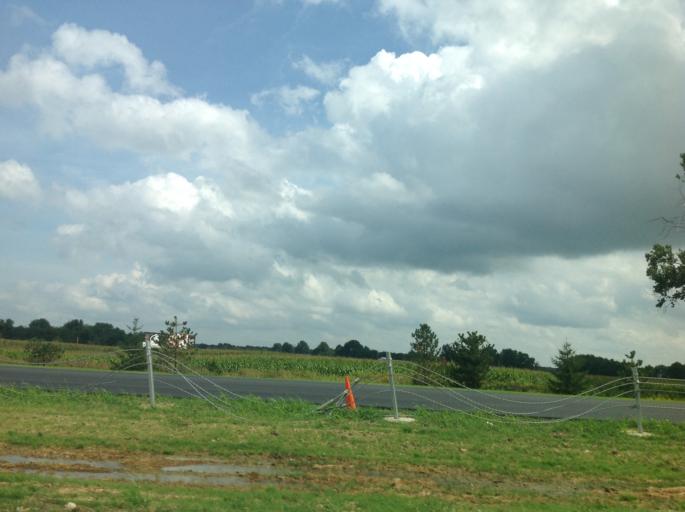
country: US
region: Ohio
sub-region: Delaware County
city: Sunbury
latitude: 40.3113
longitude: -82.9166
